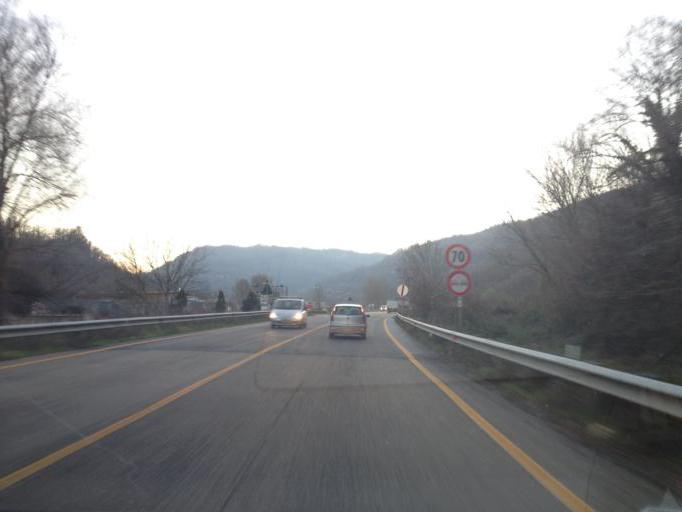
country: IT
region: The Marches
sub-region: Provincia di Ascoli Piceno
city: Arquata del Tronto
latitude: 42.7479
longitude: 13.2704
